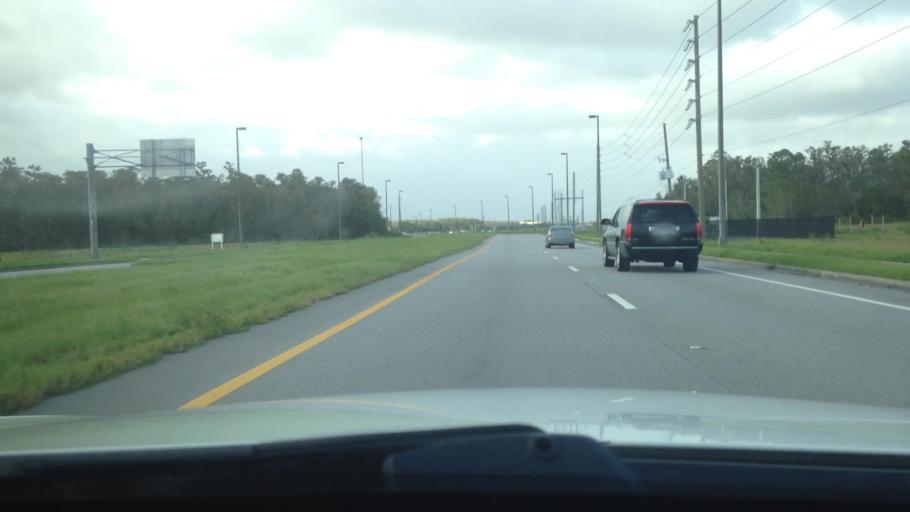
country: US
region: Florida
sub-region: Orange County
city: Conway
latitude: 28.4589
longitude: -81.2863
